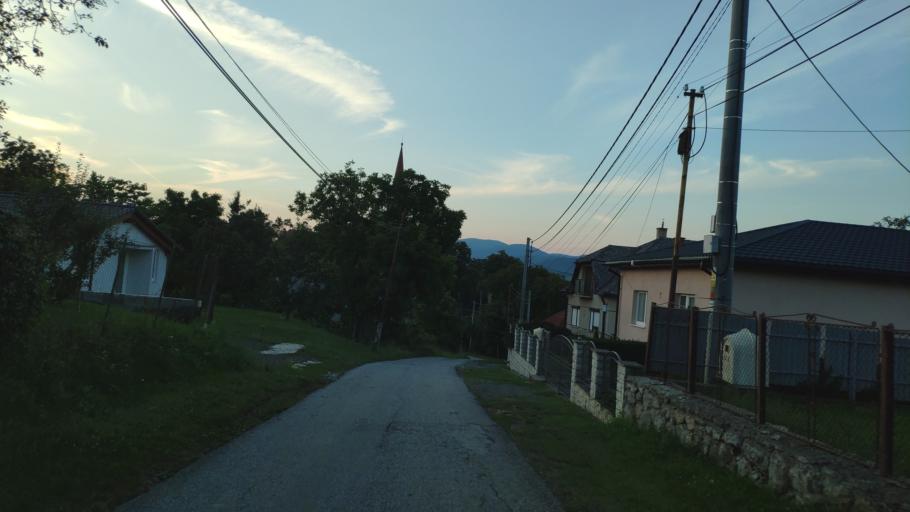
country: SK
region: Kosicky
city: Secovce
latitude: 48.5972
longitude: 21.5539
